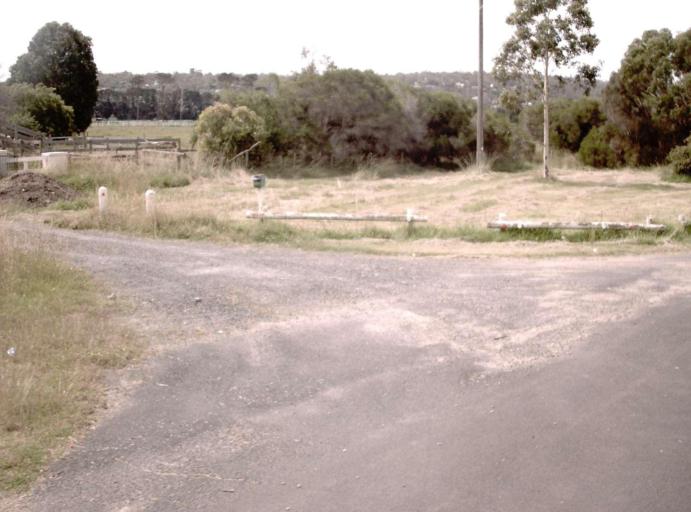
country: AU
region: Victoria
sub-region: Mornington Peninsula
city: Moorooduc
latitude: -38.2211
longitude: 145.1028
